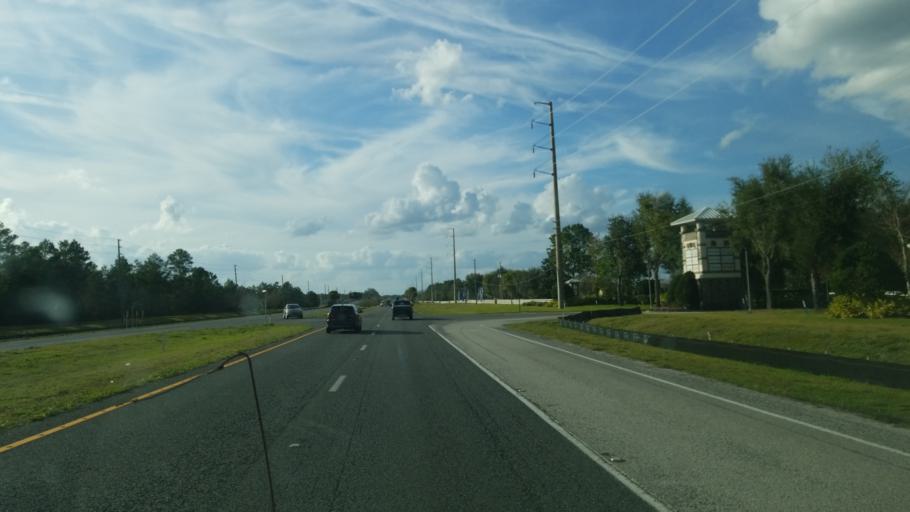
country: US
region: Florida
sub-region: Osceola County
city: Saint Cloud
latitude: 28.1874
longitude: -81.1457
